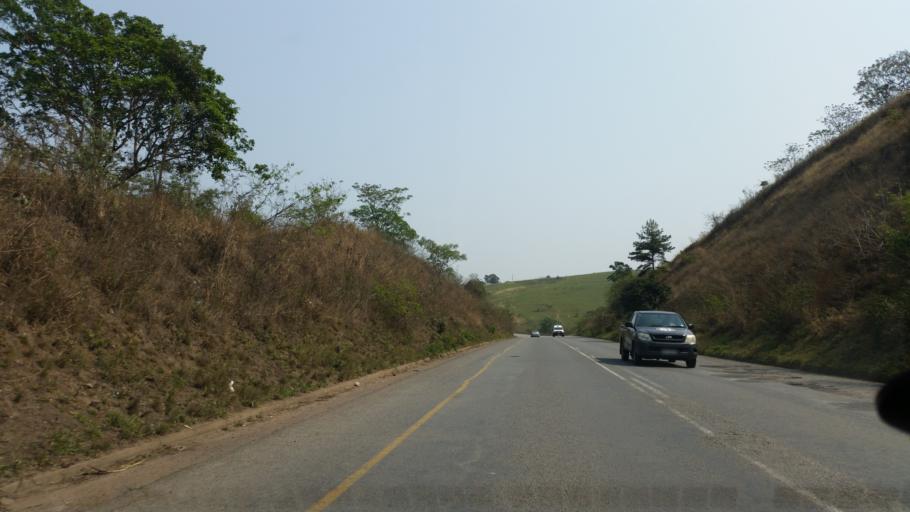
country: ZA
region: KwaZulu-Natal
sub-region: eThekwini Metropolitan Municipality
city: Mpumalanga
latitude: -29.7393
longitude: 30.6604
